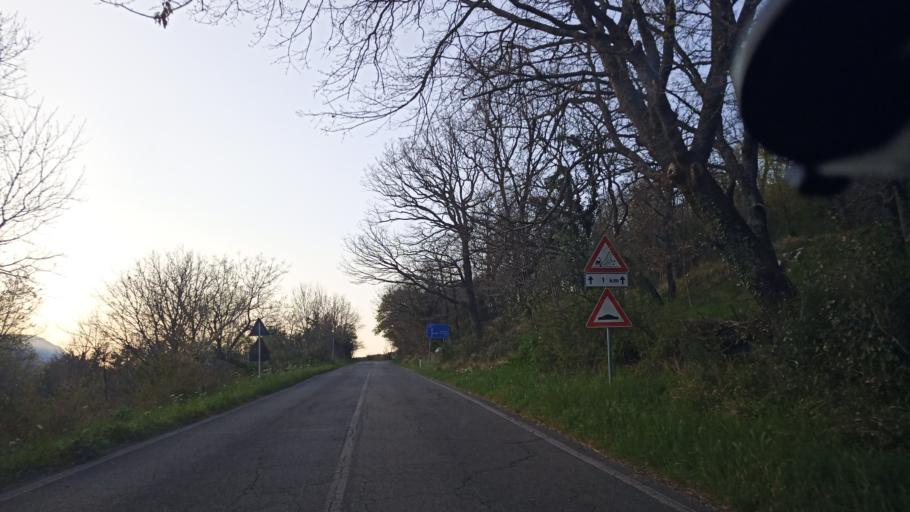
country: IT
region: Latium
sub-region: Provincia di Rieti
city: Cottanello
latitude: 42.4112
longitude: 12.6796
